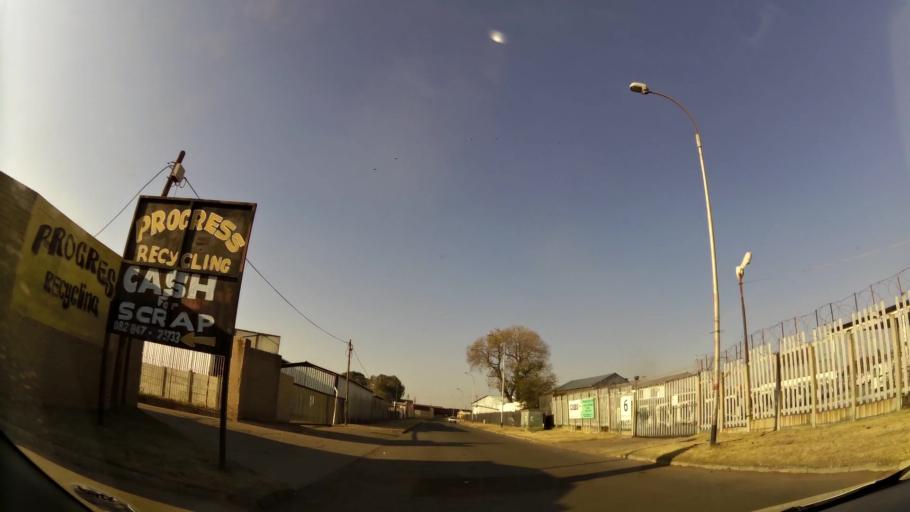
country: ZA
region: Gauteng
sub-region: West Rand District Municipality
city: Randfontein
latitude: -26.1908
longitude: 27.6924
